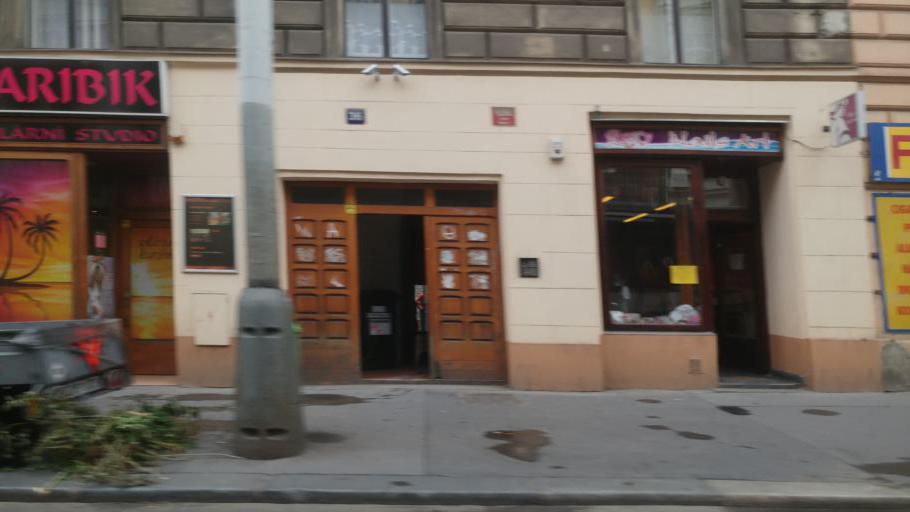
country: CZ
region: Praha
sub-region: Praha 8
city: Karlin
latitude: 50.0842
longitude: 14.4516
